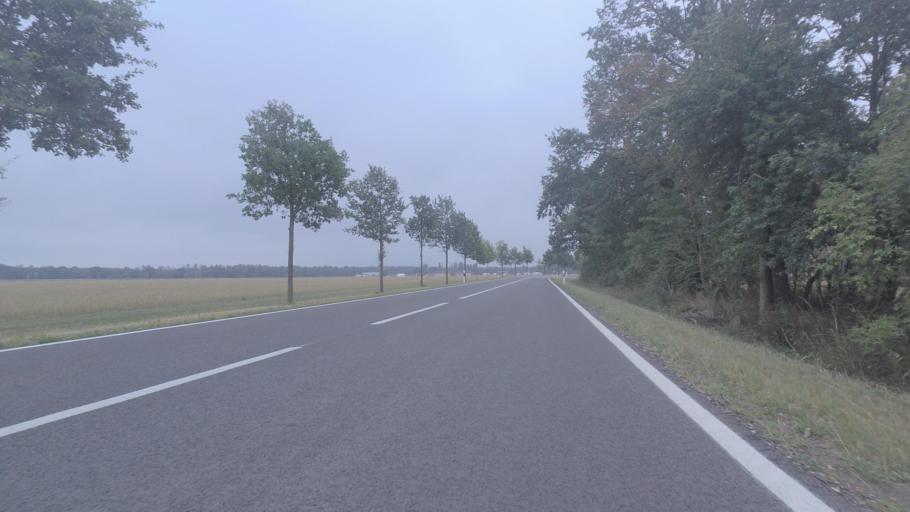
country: DE
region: Brandenburg
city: Paulinenaue
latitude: 52.6586
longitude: 12.7441
